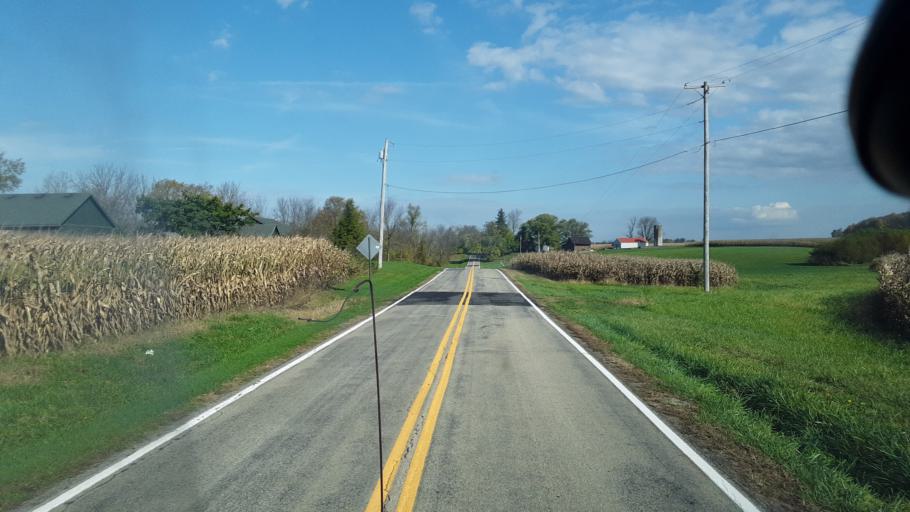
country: US
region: Ohio
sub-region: Highland County
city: Leesburg
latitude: 39.3258
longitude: -83.5859
